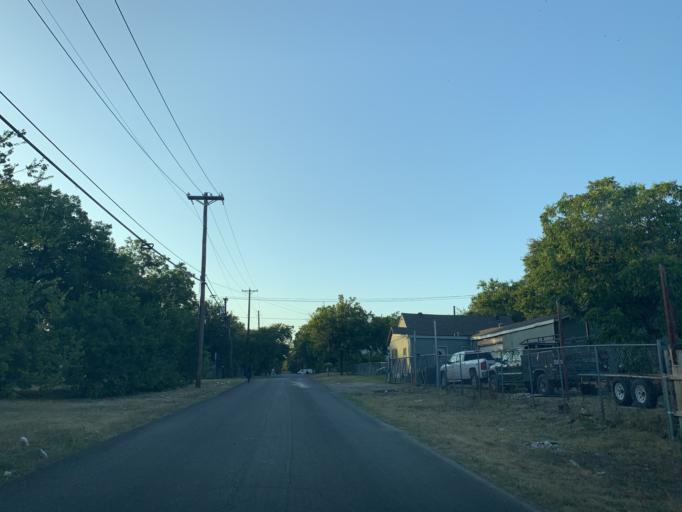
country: US
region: Texas
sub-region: Dallas County
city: Dallas
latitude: 32.7023
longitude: -96.8000
